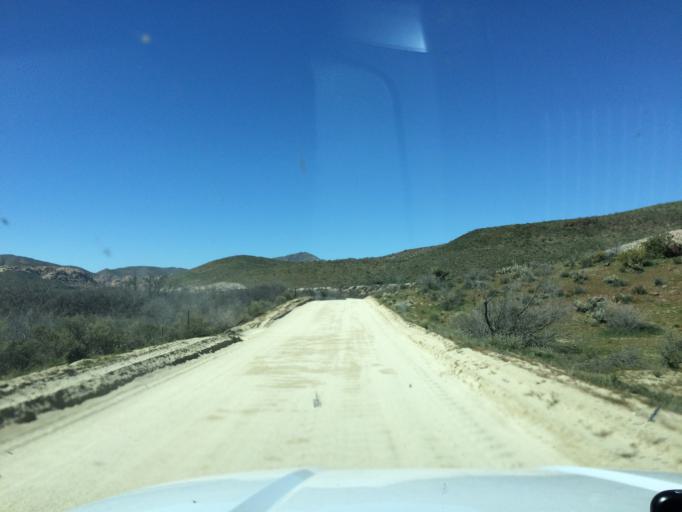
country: MX
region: Baja California
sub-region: Tecate
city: Cereso del Hongo
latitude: 32.6398
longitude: -116.1751
